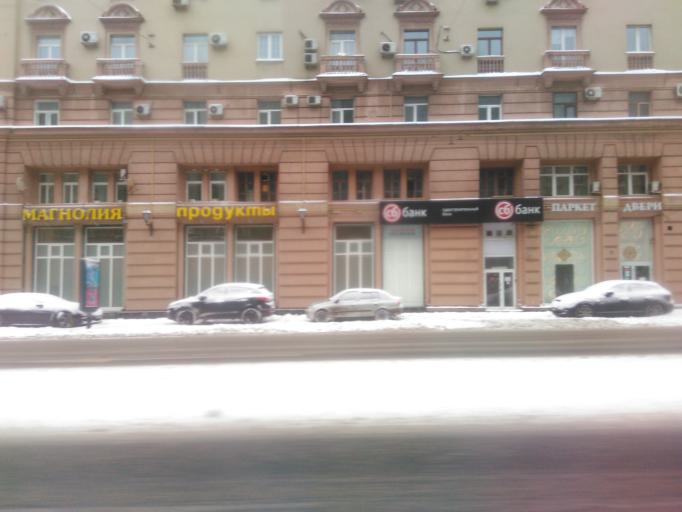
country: RU
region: Moscow
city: Mar'ina Roshcha
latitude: 55.7884
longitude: 37.6351
